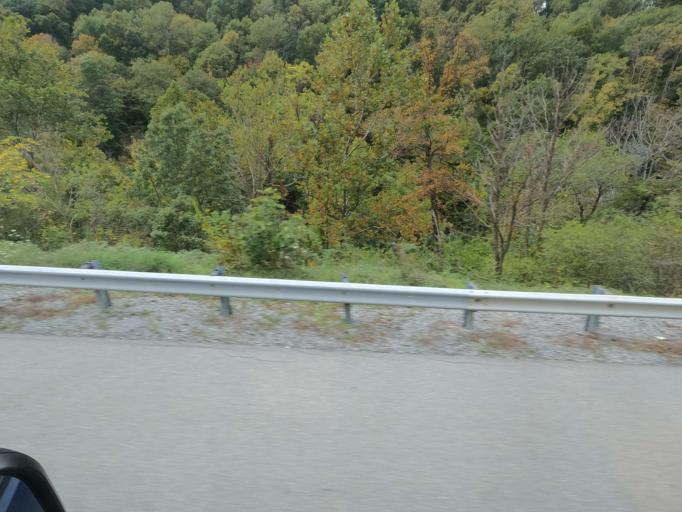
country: US
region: Tennessee
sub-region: Carter County
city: Elizabethton
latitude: 36.2942
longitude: -82.1779
